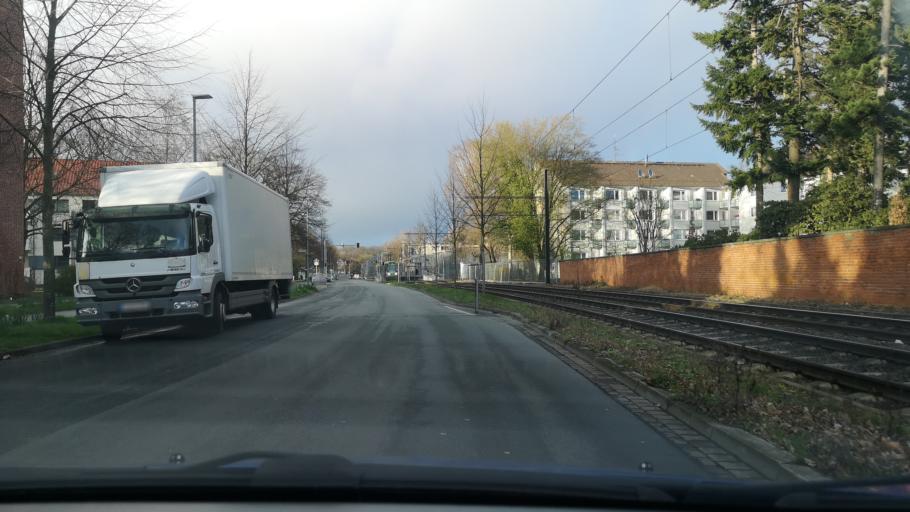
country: DE
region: Lower Saxony
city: Auf der Horst
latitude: 52.4079
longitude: 9.6618
